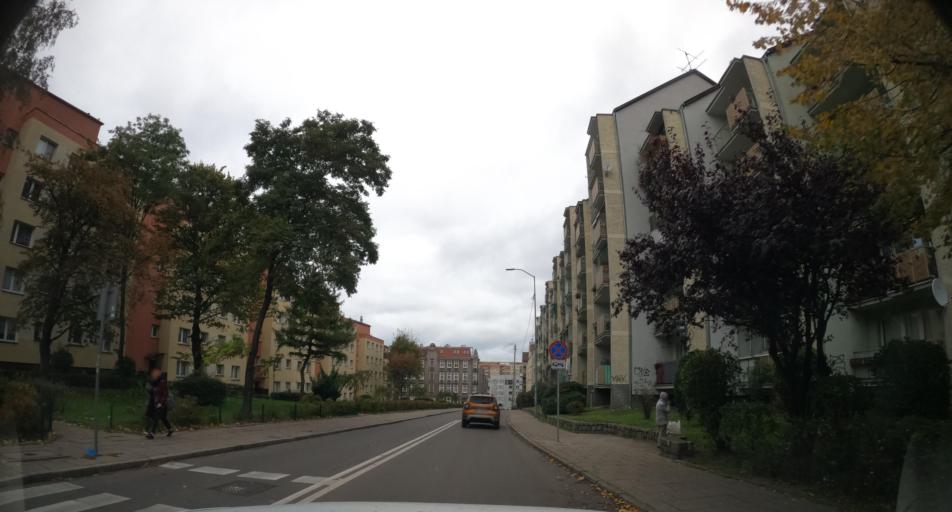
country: PL
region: West Pomeranian Voivodeship
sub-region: Szczecin
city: Szczecin
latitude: 53.4376
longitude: 14.5689
